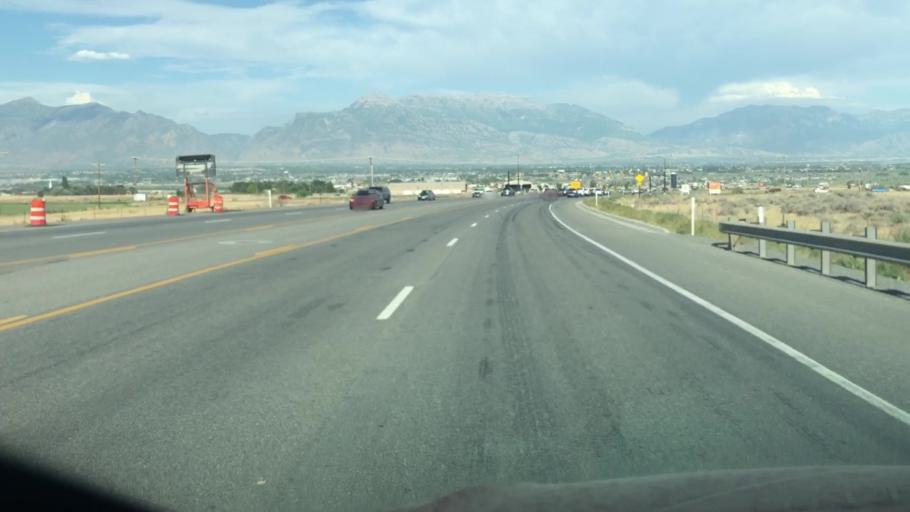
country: US
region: Utah
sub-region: Utah County
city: Saratoga Springs
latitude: 40.3867
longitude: -111.9379
